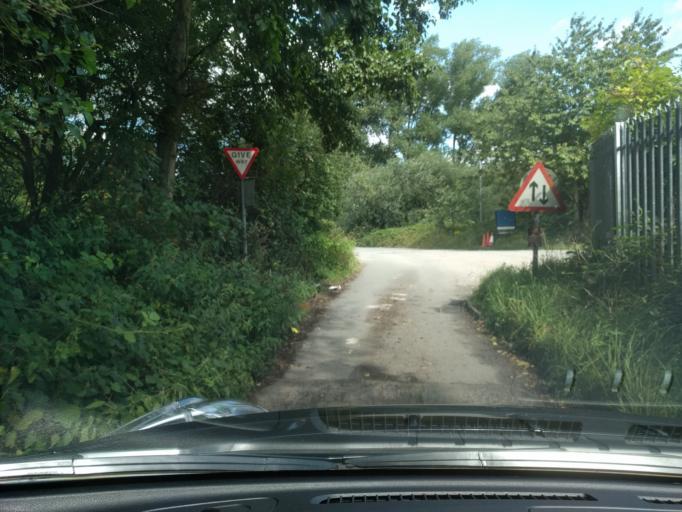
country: GB
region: England
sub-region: Warrington
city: Grappenhall
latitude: 53.3960
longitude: -2.5452
